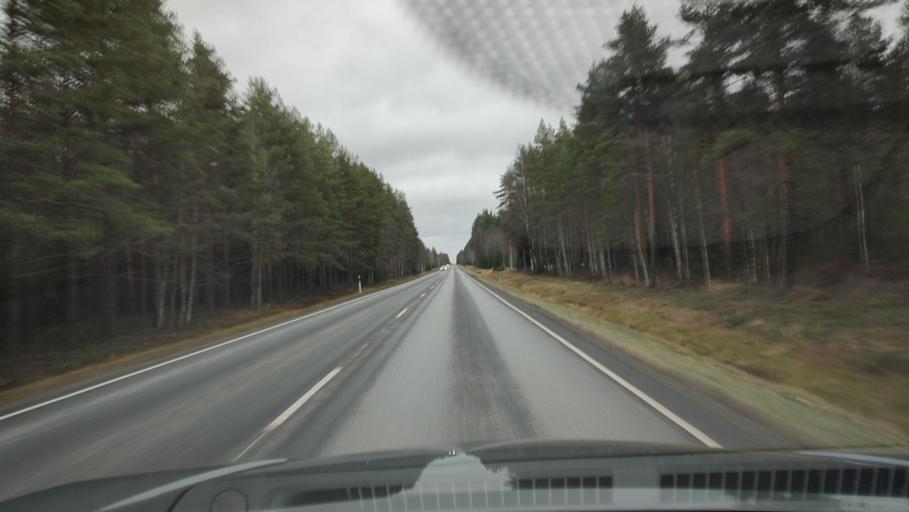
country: FI
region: Southern Ostrobothnia
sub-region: Seinaejoki
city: Kurikka
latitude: 62.5214
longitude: 22.3189
